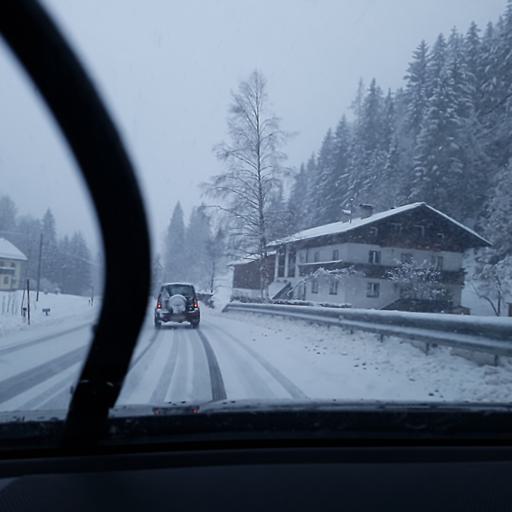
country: AT
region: Salzburg
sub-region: Politischer Bezirk Hallein
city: Abtenau
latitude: 47.5808
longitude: 13.4379
